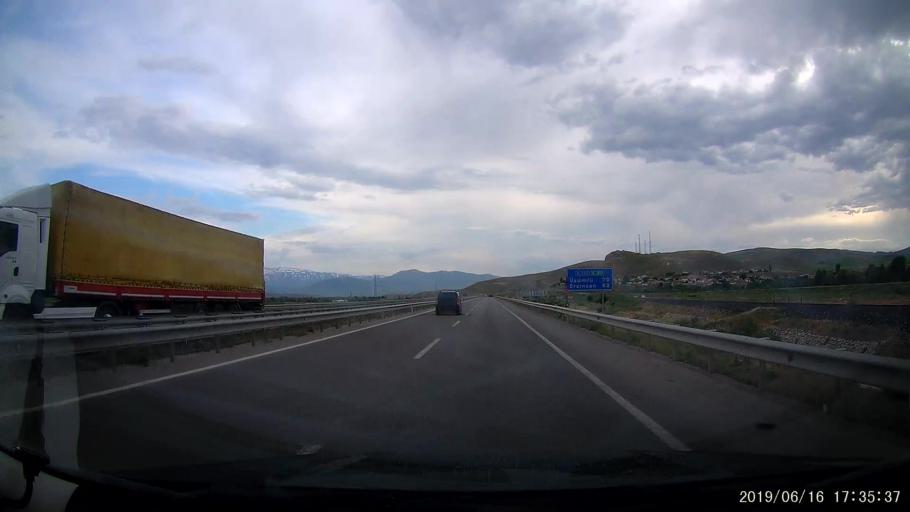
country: TR
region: Erzincan
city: Tercan
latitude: 39.7354
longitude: 40.2610
